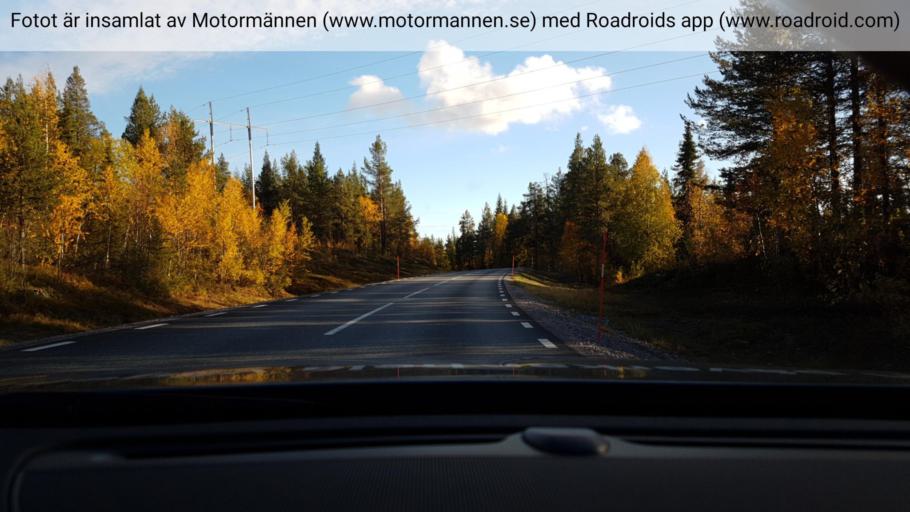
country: SE
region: Norrbotten
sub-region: Jokkmokks Kommun
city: Jokkmokk
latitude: 66.9274
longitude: 19.8248
